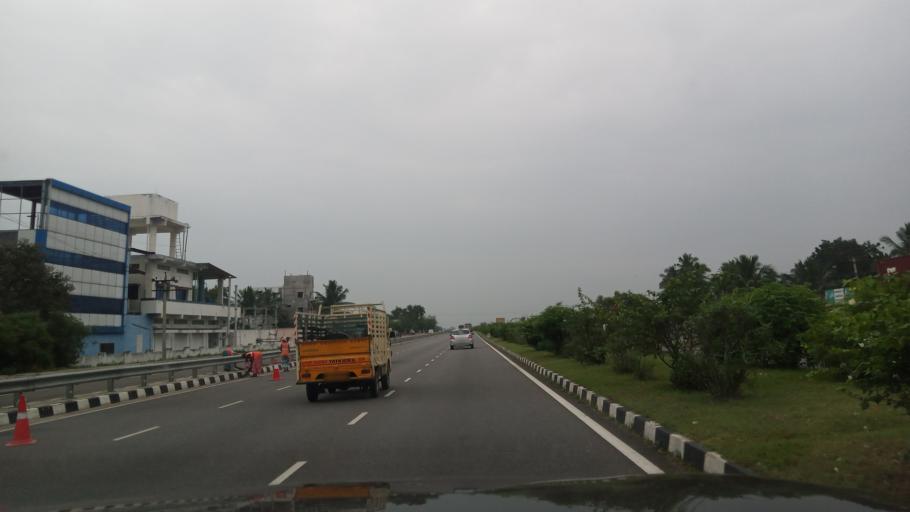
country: IN
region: Tamil Nadu
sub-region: Vellore
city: Pallikondai
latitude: 12.9122
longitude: 79.0021
